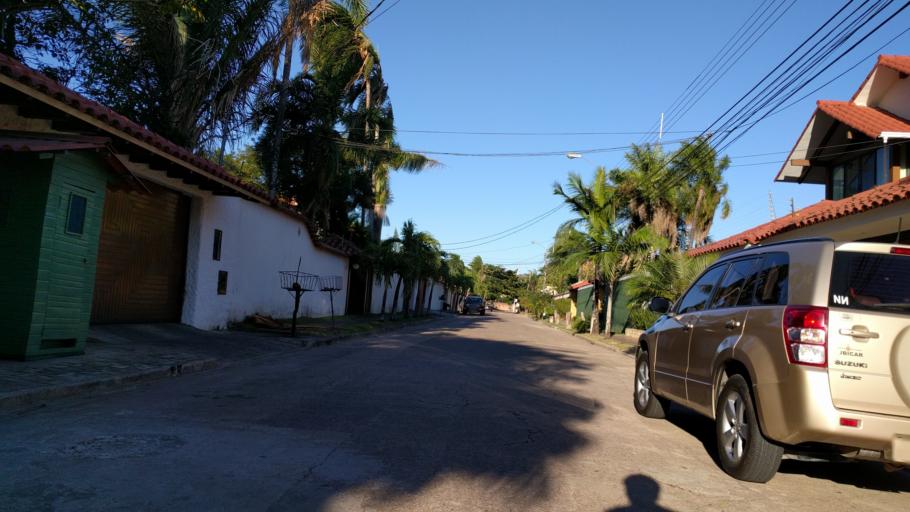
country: BO
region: Santa Cruz
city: Santa Cruz de la Sierra
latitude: -17.8043
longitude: -63.2105
